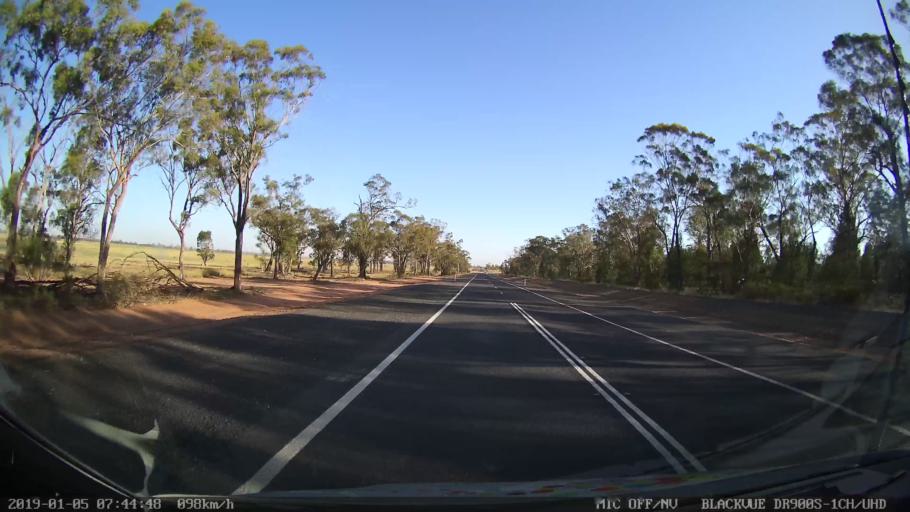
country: AU
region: New South Wales
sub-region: Gilgandra
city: Gilgandra
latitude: -31.8673
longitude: 148.6404
